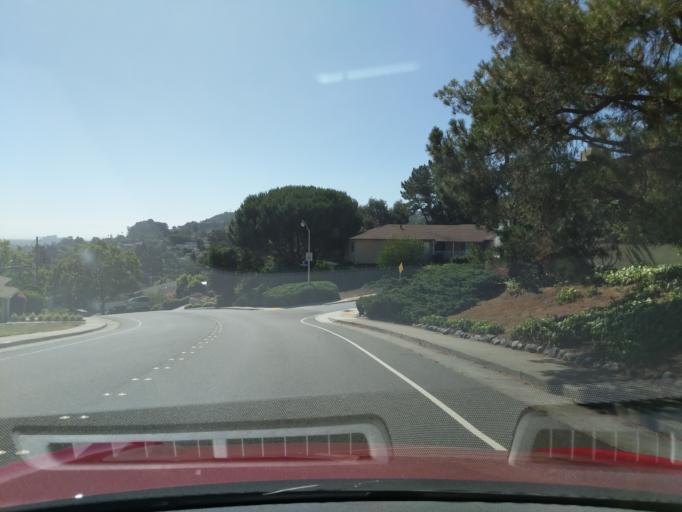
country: US
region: California
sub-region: San Mateo County
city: Highlands-Baywood Park
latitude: 37.5298
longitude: -122.3162
